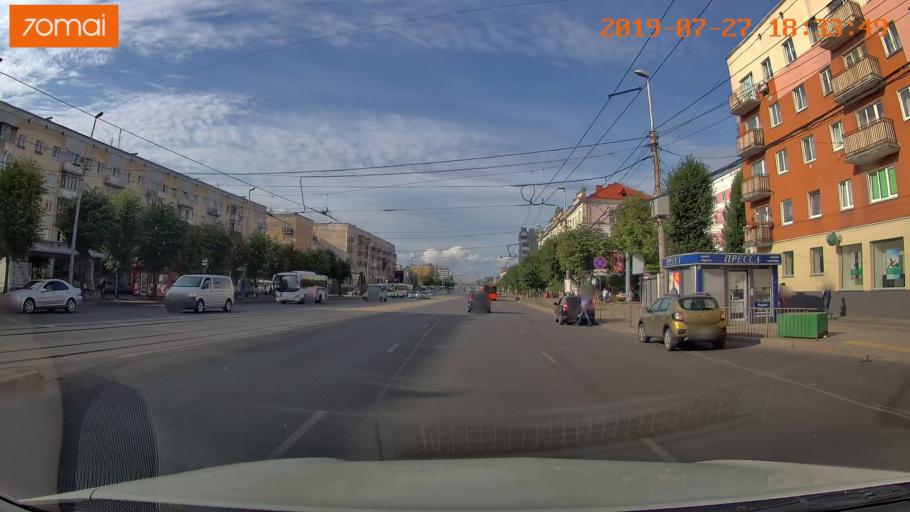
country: RU
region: Kaliningrad
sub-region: Gorod Kaliningrad
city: Kaliningrad
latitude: 54.7000
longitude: 20.5037
